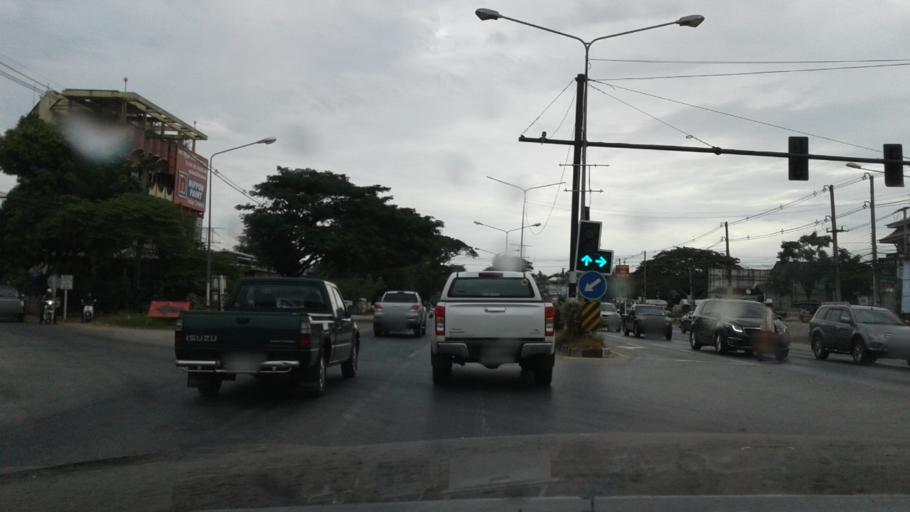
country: TH
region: Changwat Udon Thani
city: Nong Wua So
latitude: 17.2726
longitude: 102.6004
